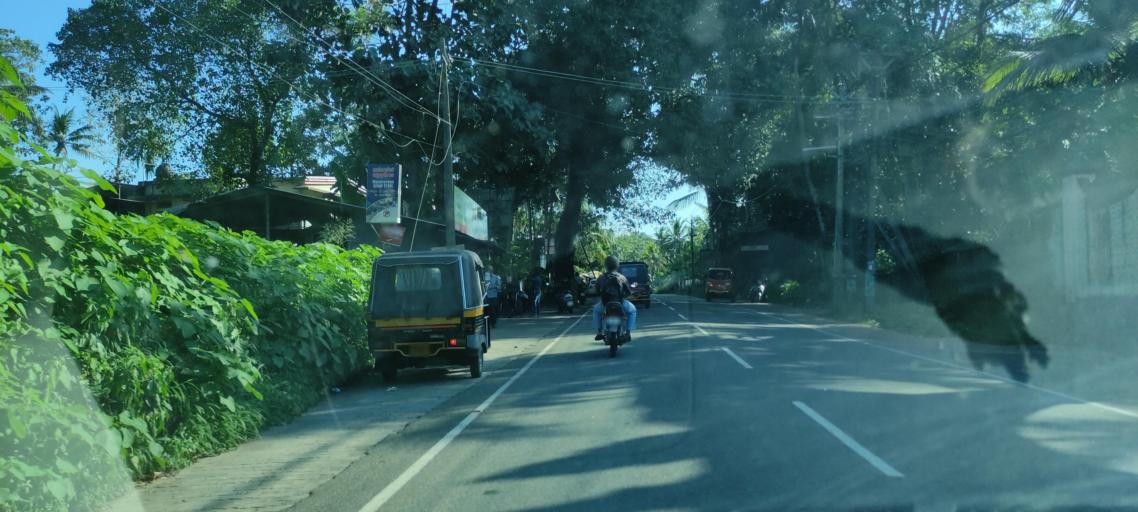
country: IN
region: Kerala
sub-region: Pattanamtitta
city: Pathanamthitta
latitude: 9.2358
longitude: 76.7552
